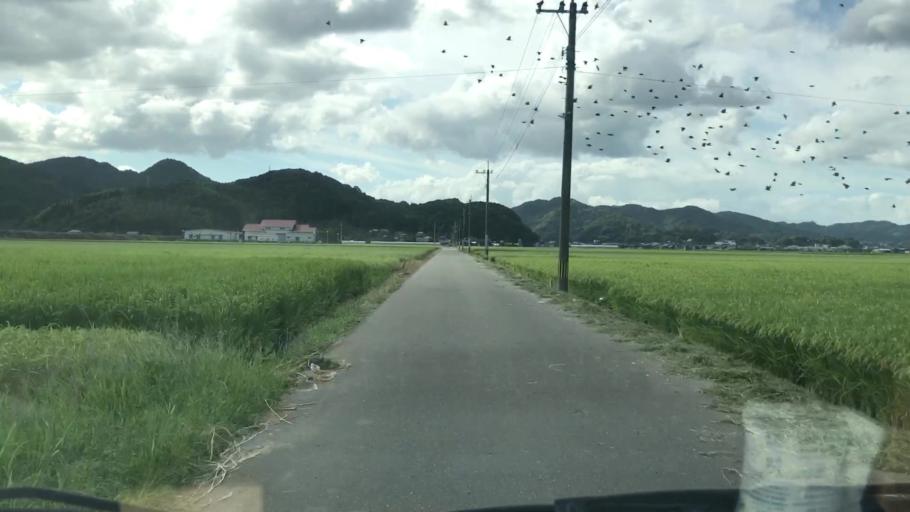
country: JP
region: Saga Prefecture
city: Kashima
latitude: 33.1146
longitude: 130.0800
